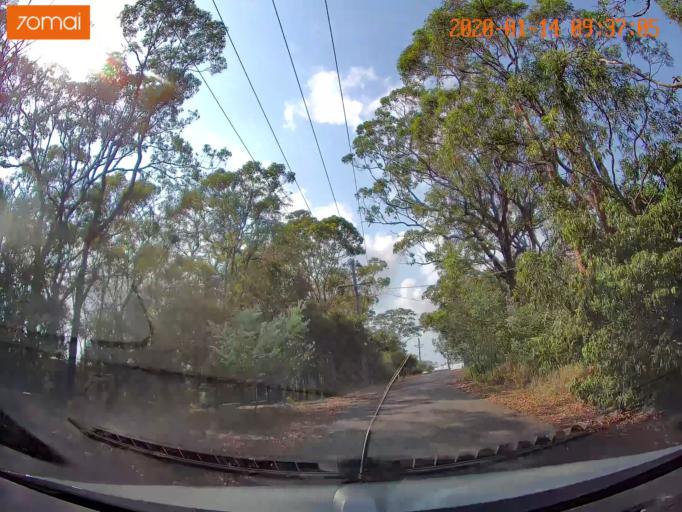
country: AU
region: New South Wales
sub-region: Wyong Shire
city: Kingfisher Shores
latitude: -33.1153
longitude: 151.5590
